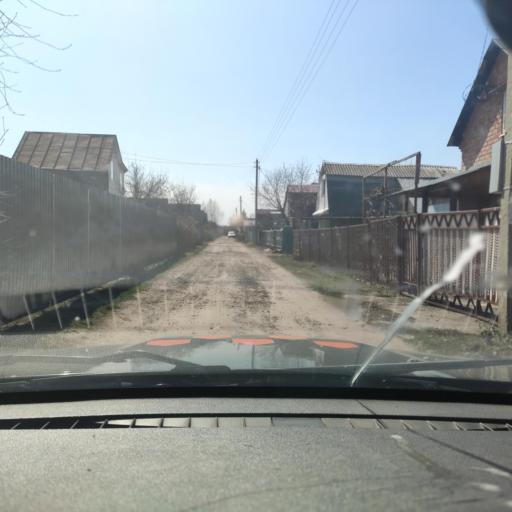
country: RU
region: Samara
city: Tol'yatti
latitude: 53.5844
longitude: 49.3145
